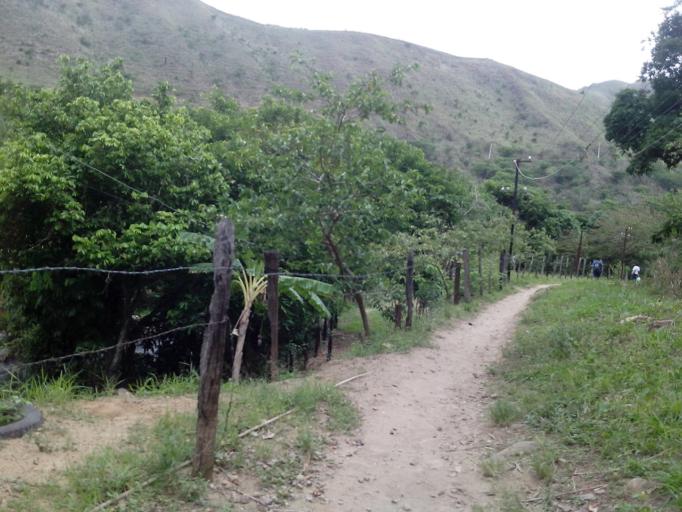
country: BR
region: Rio de Janeiro
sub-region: Miguel Pereira
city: Miguel Pereira
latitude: -22.5090
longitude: -43.5229
